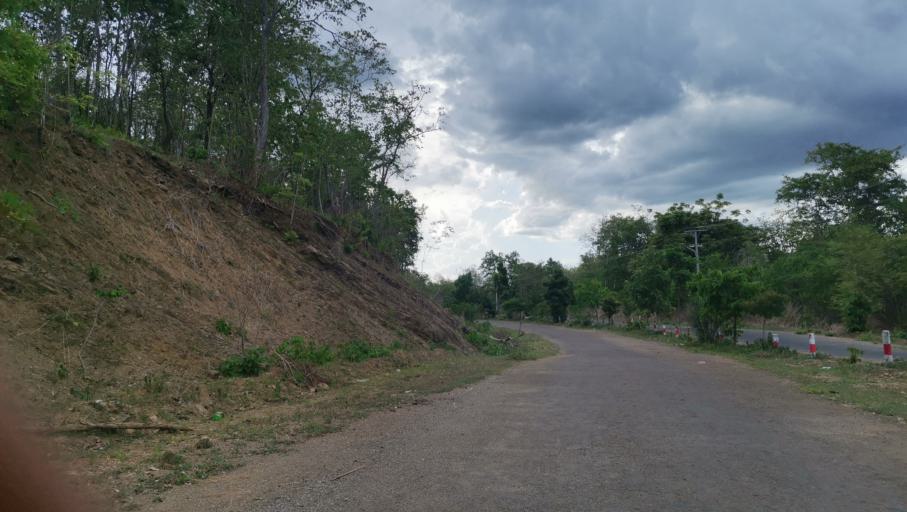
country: MM
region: Magway
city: Minbu
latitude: 20.1041
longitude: 94.5478
